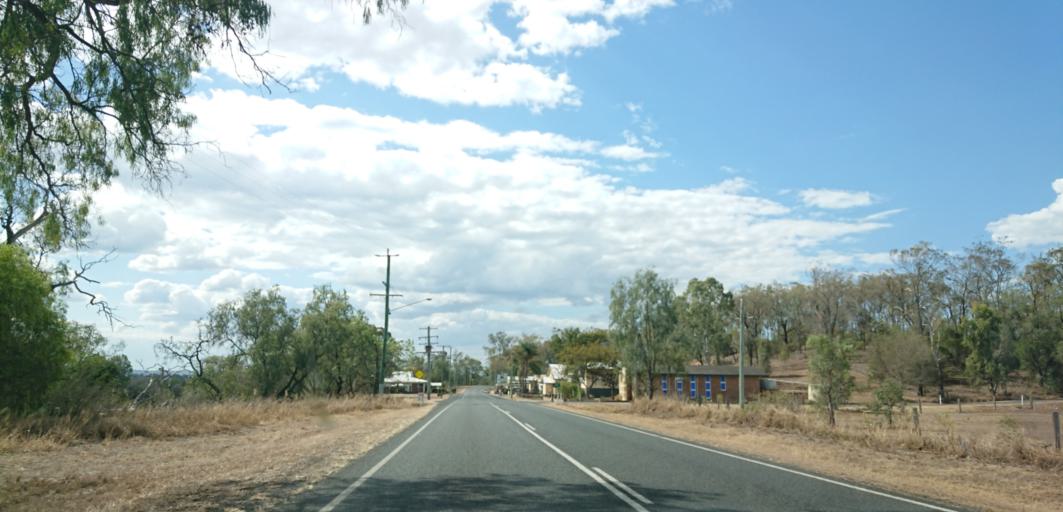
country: AU
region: Queensland
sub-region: Lockyer Valley
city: Gatton
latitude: -27.6327
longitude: 152.1873
